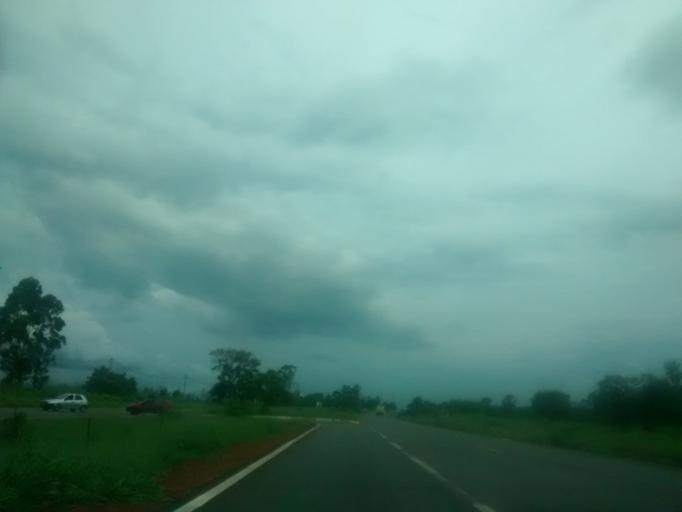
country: BR
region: Federal District
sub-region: Brasilia
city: Brasilia
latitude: -15.8920
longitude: -47.8204
